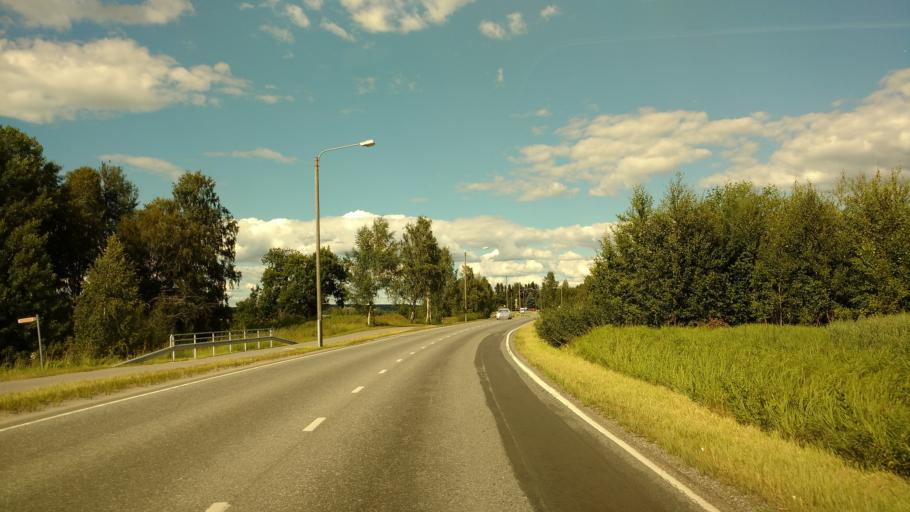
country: FI
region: Varsinais-Suomi
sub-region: Salo
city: Salo
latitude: 60.3977
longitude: 23.1568
